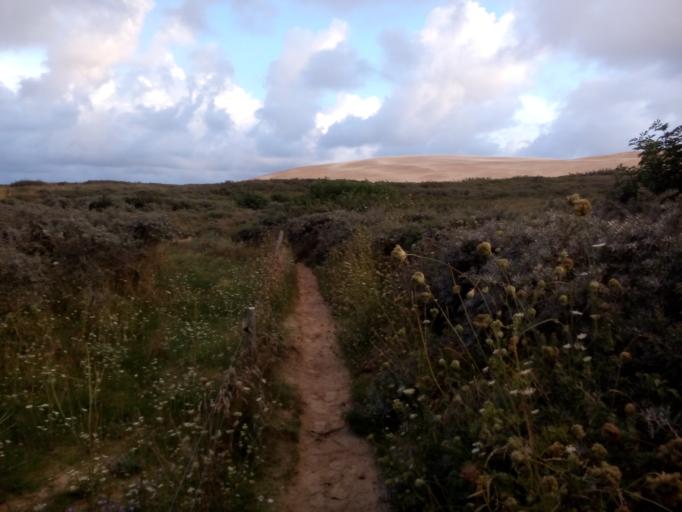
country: DK
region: North Denmark
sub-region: Hjorring Kommune
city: Vra
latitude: 57.4502
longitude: 9.7779
